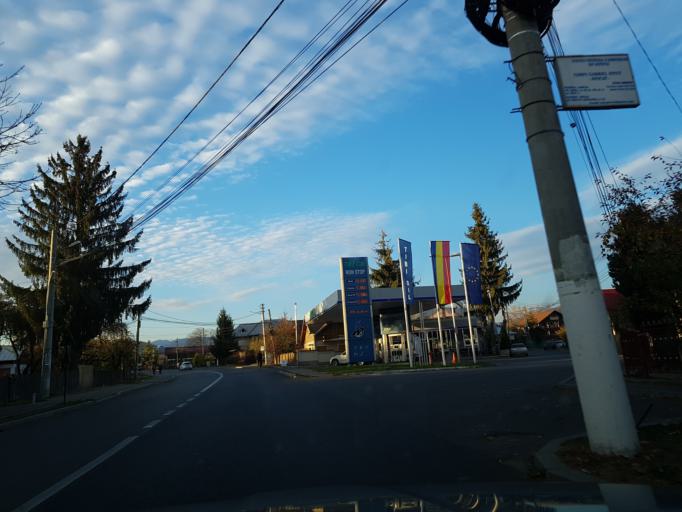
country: RO
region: Prahova
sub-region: Oras Breaza
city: Breaza
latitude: 45.1838
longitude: 25.6663
